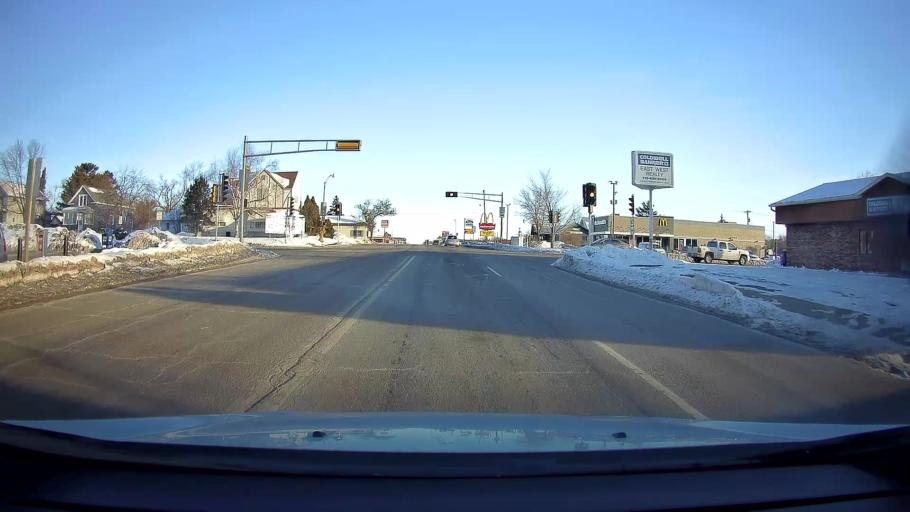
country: US
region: Wisconsin
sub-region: Washburn County
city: Spooner
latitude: 45.8226
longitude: -91.8912
